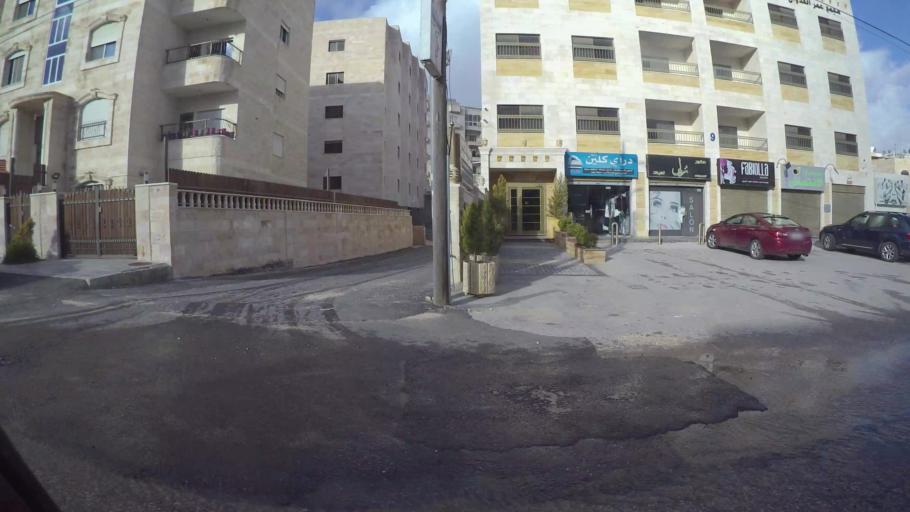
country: JO
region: Amman
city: Al Jubayhah
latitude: 32.0557
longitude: 35.8969
